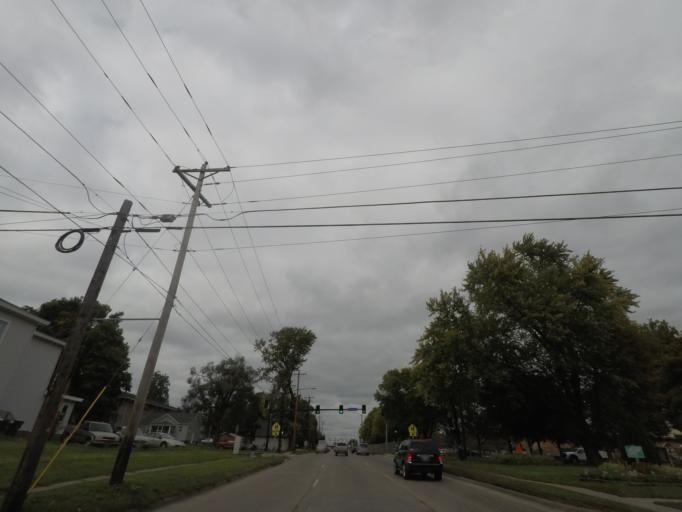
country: US
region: Iowa
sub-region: Polk County
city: Des Moines
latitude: 41.5914
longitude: -93.5944
